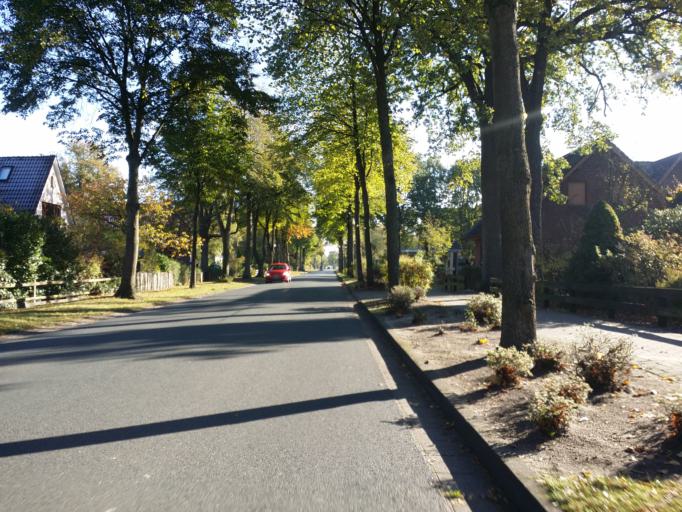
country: DE
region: Lower Saxony
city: Wilstedt
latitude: 53.1947
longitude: 9.1043
